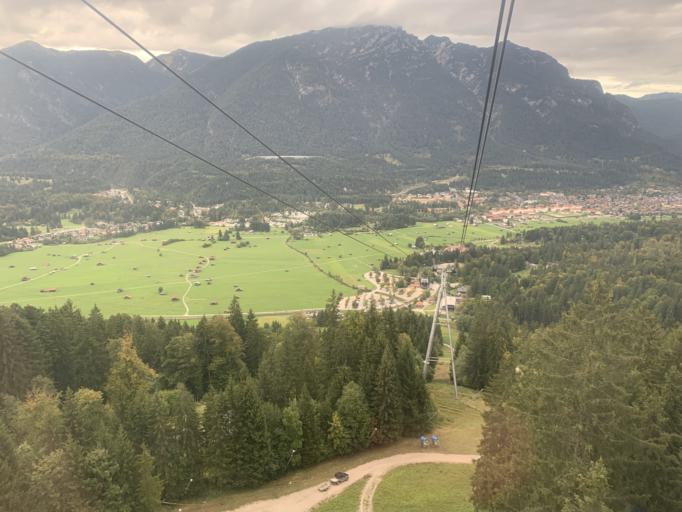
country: DE
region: Bavaria
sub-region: Upper Bavaria
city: Garmisch-Partenkirchen
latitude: 47.4640
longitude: 11.0651
